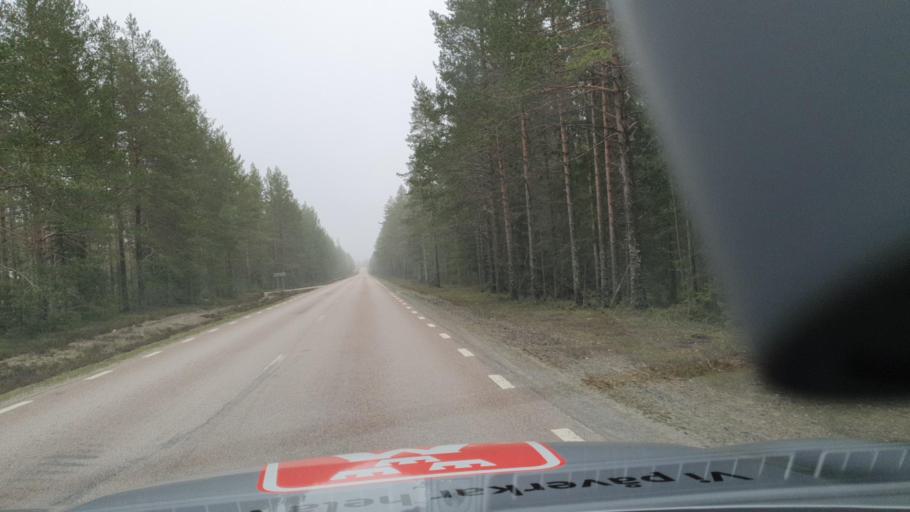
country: SE
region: Vaesternorrland
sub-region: OErnskoeldsviks Kommun
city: Husum
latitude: 63.4257
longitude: 18.9592
